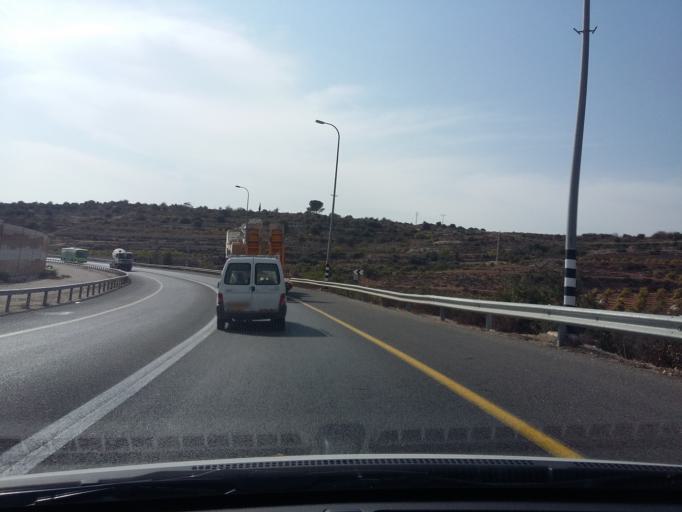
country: PS
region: West Bank
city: Al Khadir
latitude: 31.6952
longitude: 35.1552
